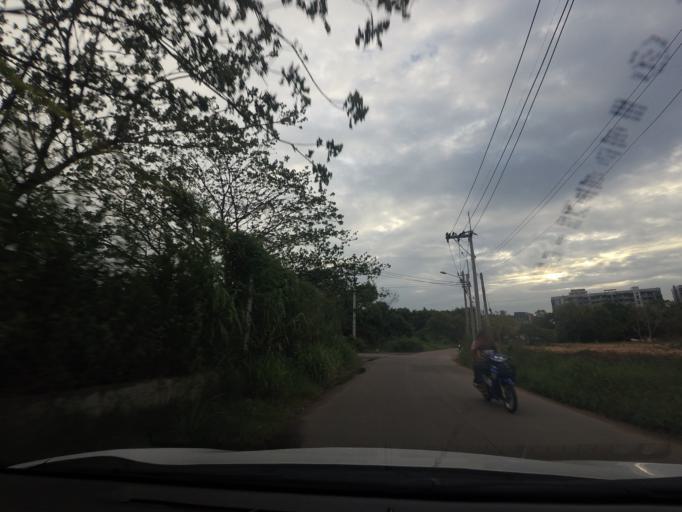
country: TH
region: Chon Buri
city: Phatthaya
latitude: 12.8989
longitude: 100.8829
